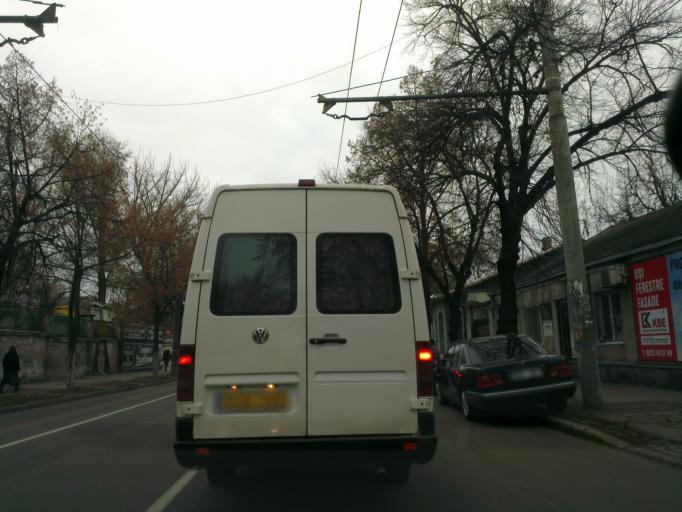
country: MD
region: Chisinau
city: Chisinau
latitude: 47.0138
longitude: 28.8399
